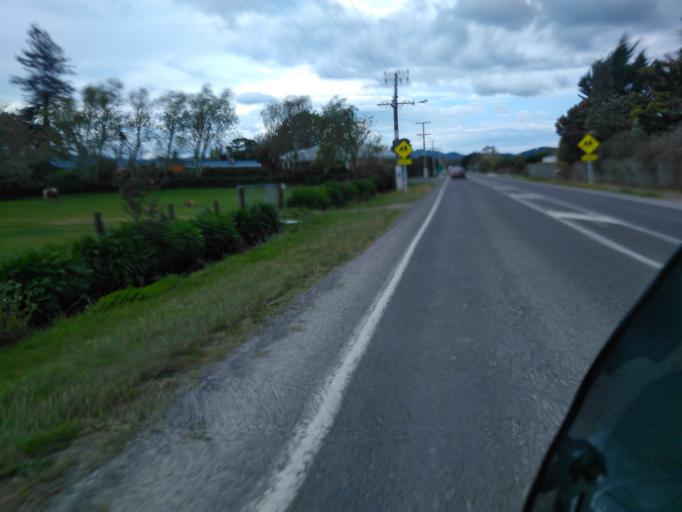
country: NZ
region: Gisborne
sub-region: Gisborne District
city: Gisborne
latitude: -38.6521
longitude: 177.9594
